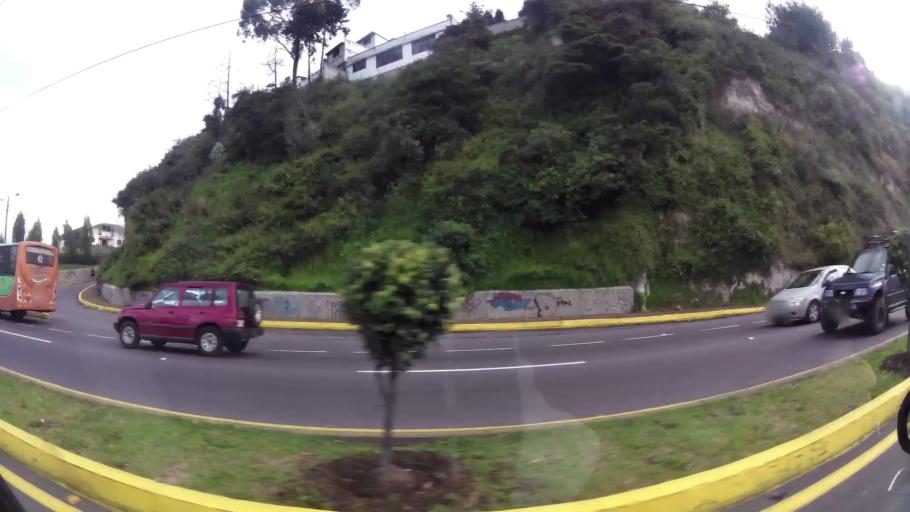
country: EC
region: Pichincha
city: Quito
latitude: -0.2275
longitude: -78.4870
